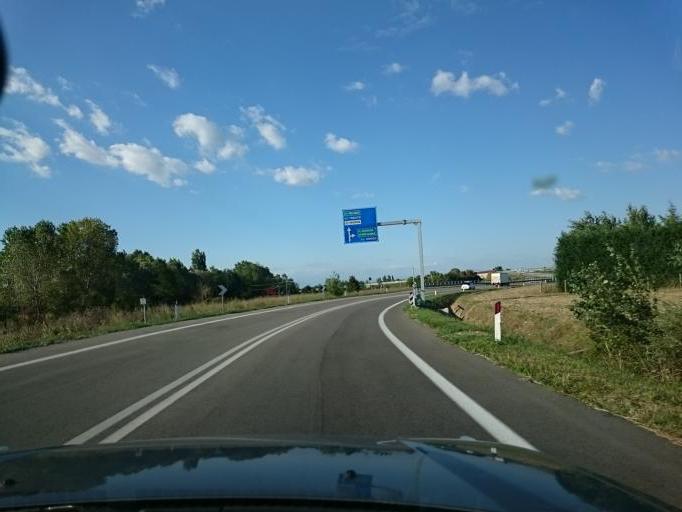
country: IT
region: Veneto
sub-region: Provincia di Padova
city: Tencarola
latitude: 45.3780
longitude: 11.8252
